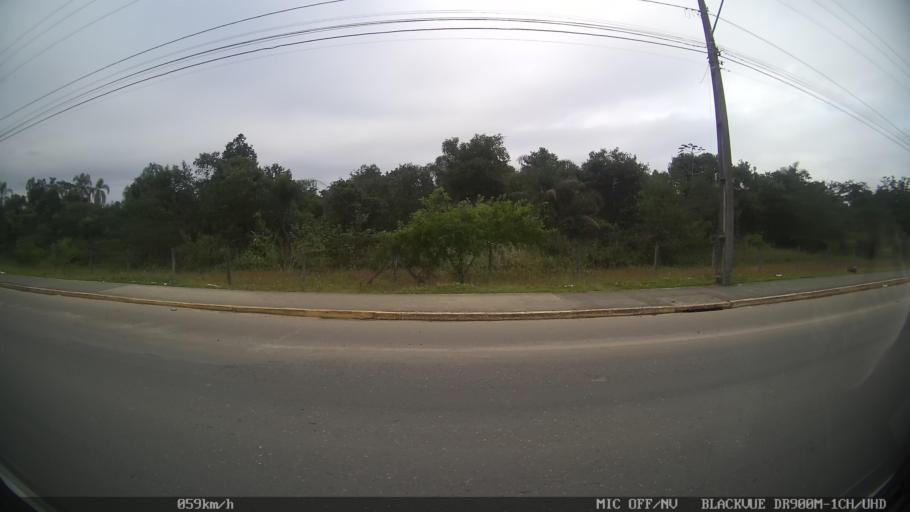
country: BR
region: Santa Catarina
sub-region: Joinville
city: Joinville
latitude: -26.3380
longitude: -48.8869
